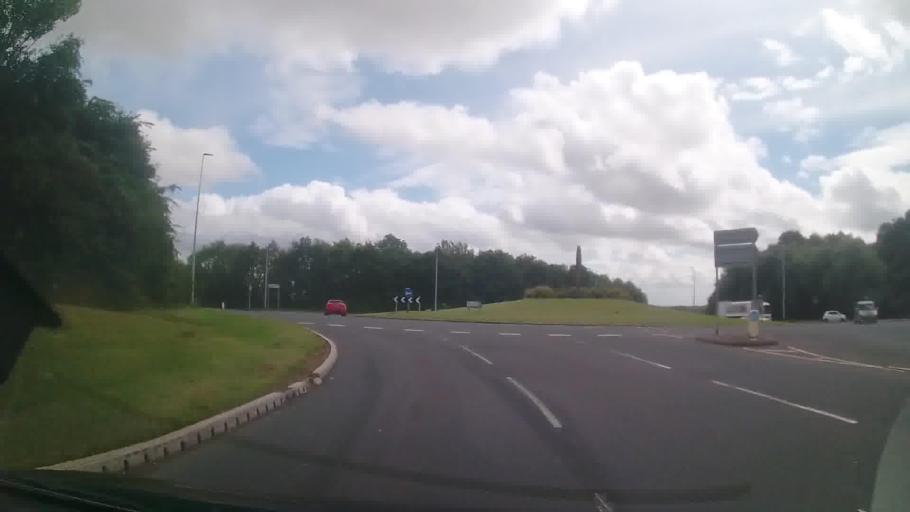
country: GB
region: England
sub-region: Telford and Wrekin
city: Oakengates
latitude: 52.6953
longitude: -2.4209
